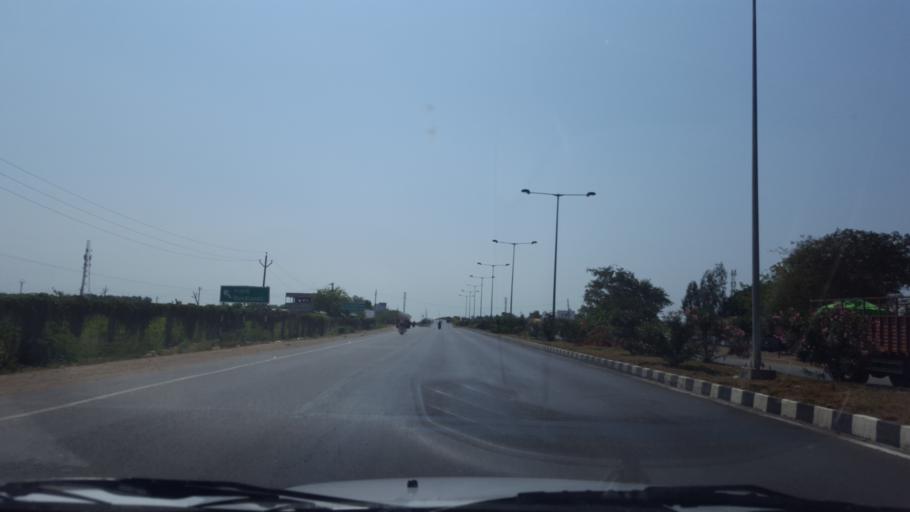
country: IN
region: Andhra Pradesh
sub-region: Prakasam
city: Addanki
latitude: 15.6641
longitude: 80.0154
